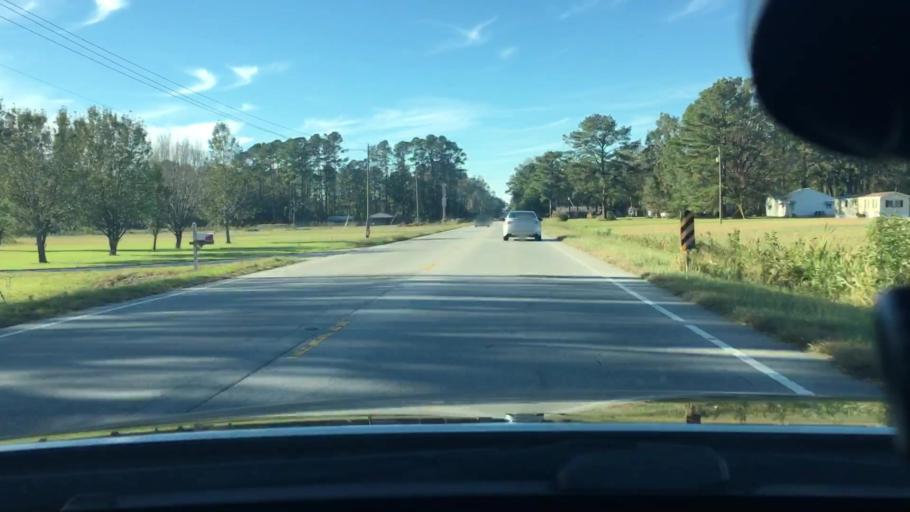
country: US
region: North Carolina
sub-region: Craven County
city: Vanceboro
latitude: 35.2562
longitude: -77.0960
